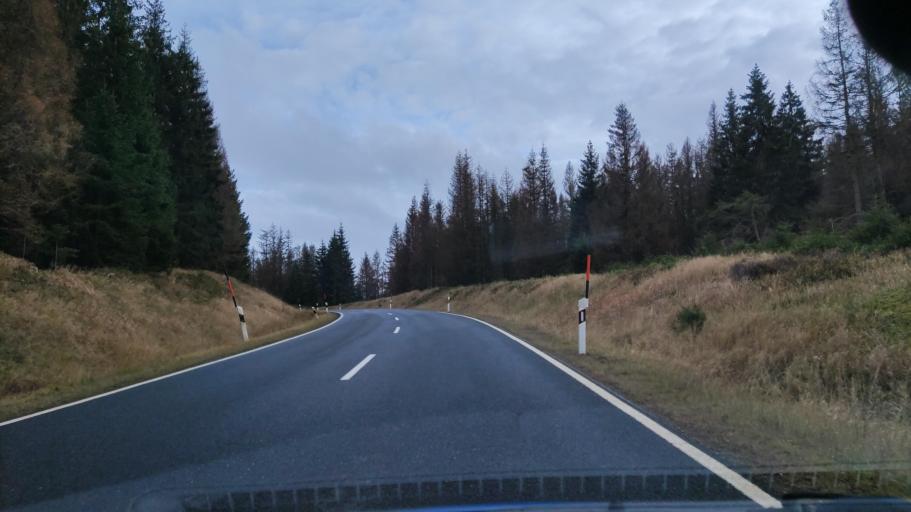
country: DE
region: Lower Saxony
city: Sankt Andreasberg
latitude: 51.7644
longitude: 10.5009
